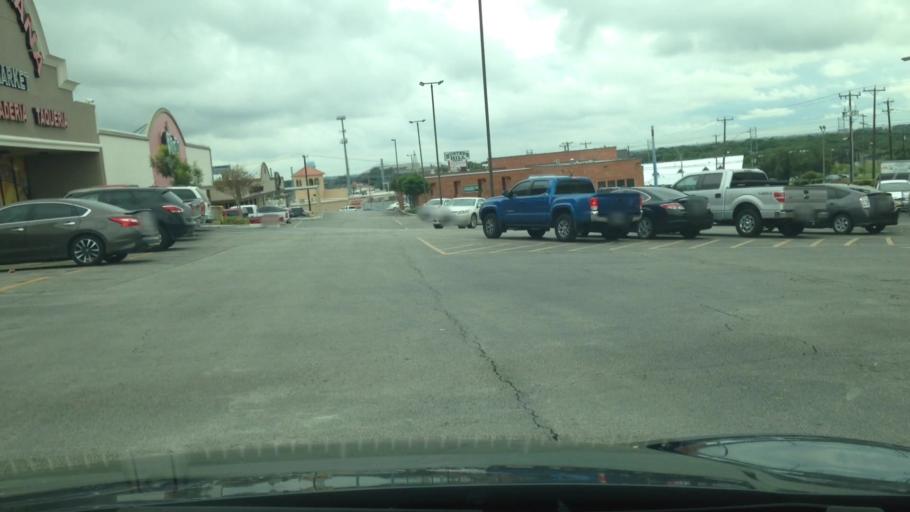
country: US
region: Texas
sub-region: Bexar County
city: Castle Hills
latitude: 29.5435
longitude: -98.5279
